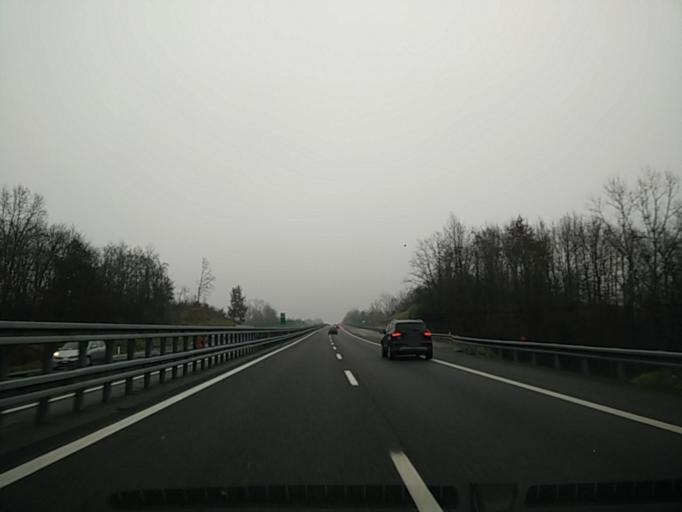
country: IT
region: Piedmont
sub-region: Provincia di Asti
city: Revigliasco d'Asti
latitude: 44.9026
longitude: 8.1433
